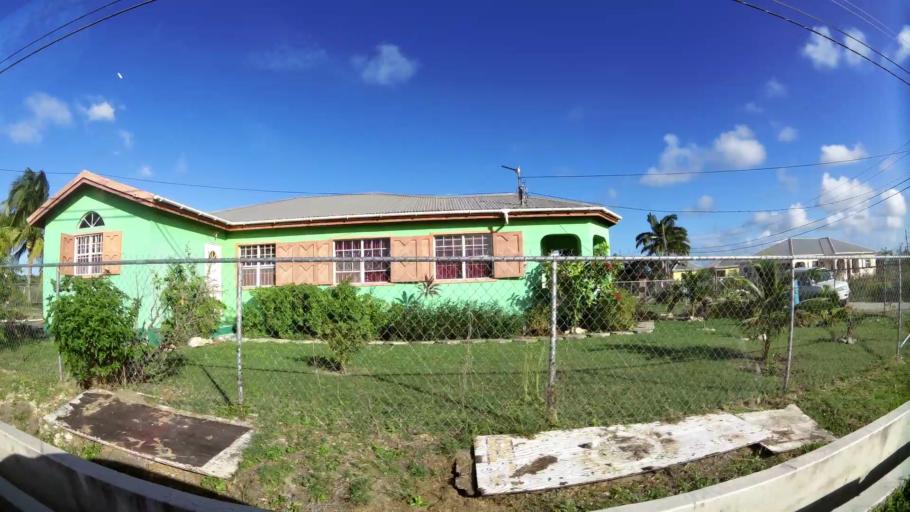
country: AG
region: Saint George
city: Piggotts
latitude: 17.1171
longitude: -61.8024
